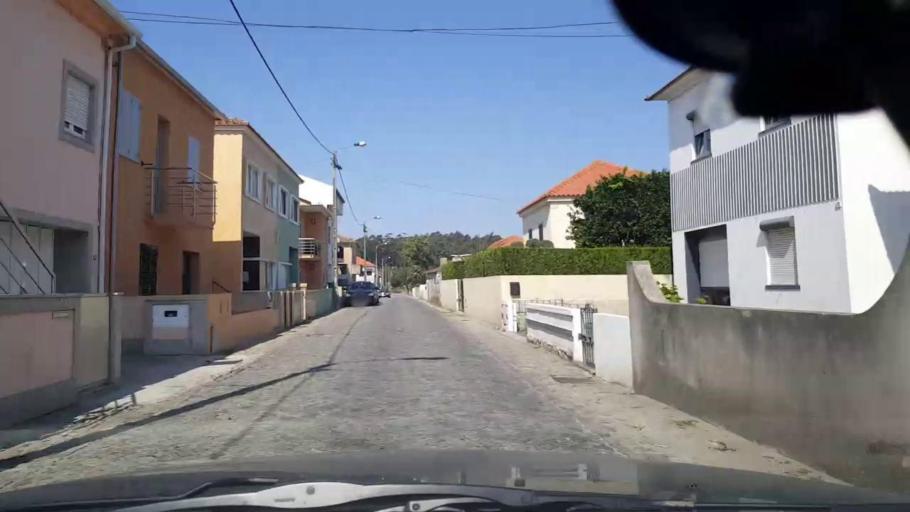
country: PT
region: Porto
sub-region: Vila do Conde
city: Vila do Conde
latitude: 41.3625
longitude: -8.7271
